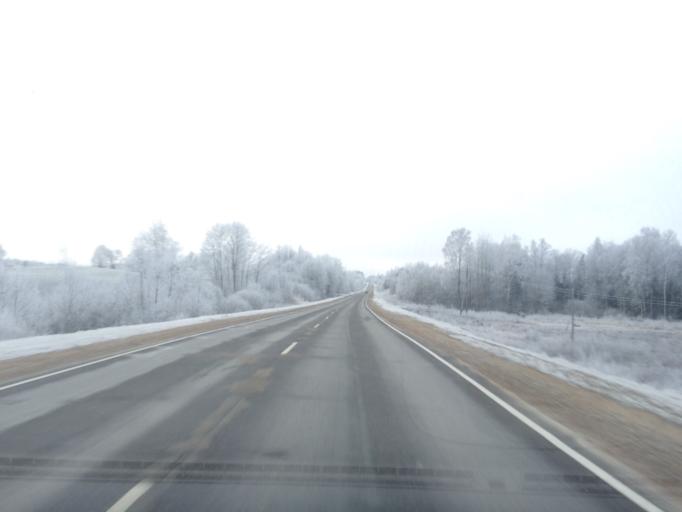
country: LV
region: Rezekne
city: Rezekne
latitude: 56.6118
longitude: 27.4440
